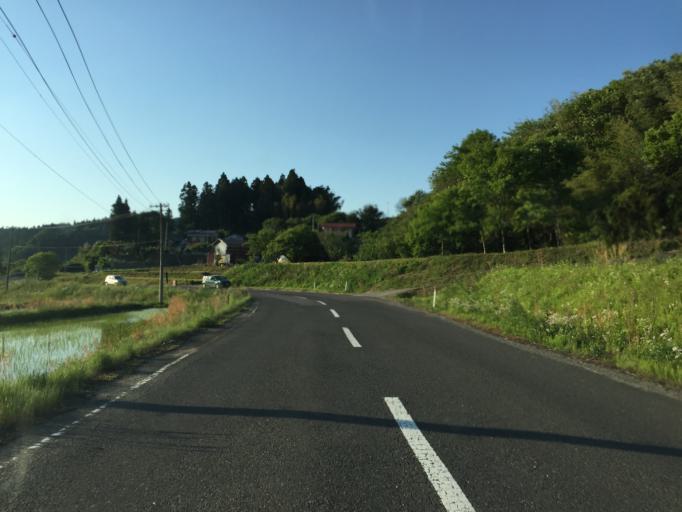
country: JP
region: Fukushima
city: Ishikawa
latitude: 37.0395
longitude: 140.4356
